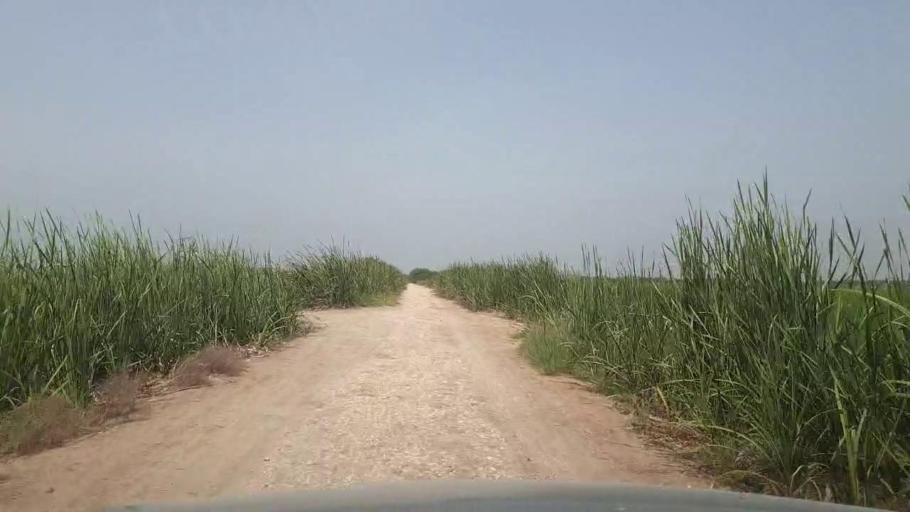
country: PK
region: Sindh
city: Garhi Yasin
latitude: 27.9422
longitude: 68.4302
